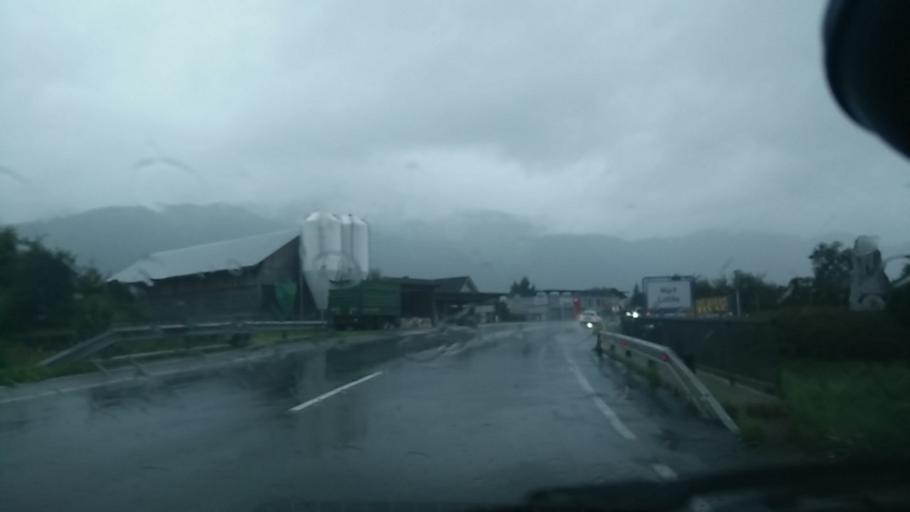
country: AT
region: Carinthia
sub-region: Politischer Bezirk Villach Land
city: Finkenstein am Faaker See
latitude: 46.5586
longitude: 13.7990
